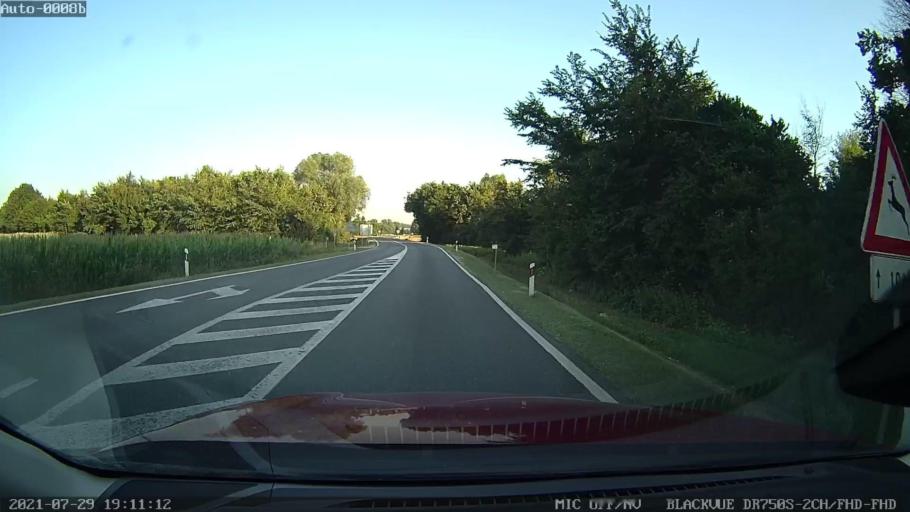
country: HR
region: Varazdinska
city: Jalzabet
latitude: 46.2811
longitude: 16.5072
